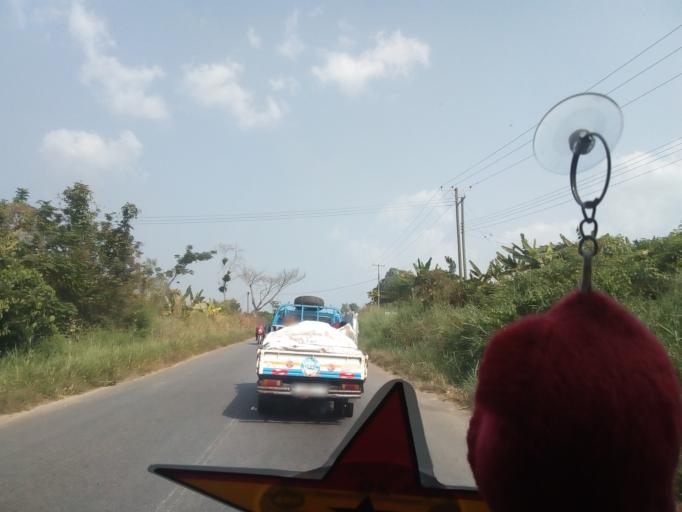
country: GH
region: Eastern
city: Suhum
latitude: 6.0441
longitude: -0.4235
